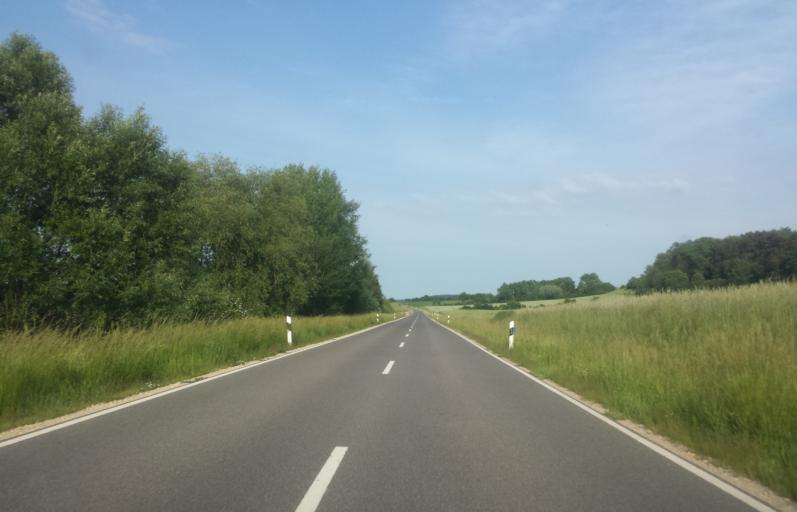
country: DE
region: Bavaria
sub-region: Upper Franconia
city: Frensdorf
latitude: 49.8187
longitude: 10.8220
